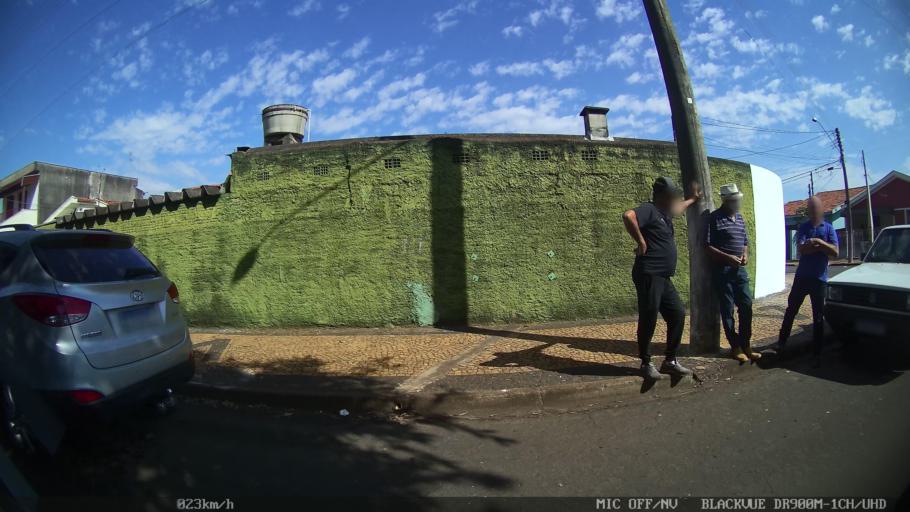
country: BR
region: Sao Paulo
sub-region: Americana
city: Americana
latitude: -22.7390
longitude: -47.2993
